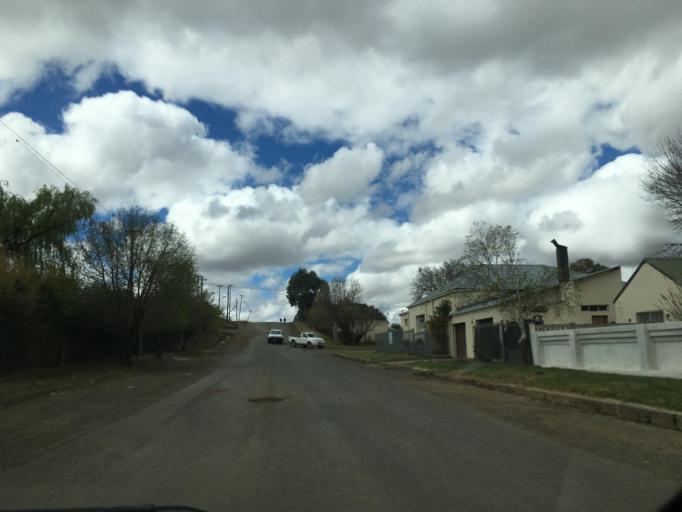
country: ZA
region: Eastern Cape
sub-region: Chris Hani District Municipality
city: Elliot
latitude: -31.3314
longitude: 27.8476
